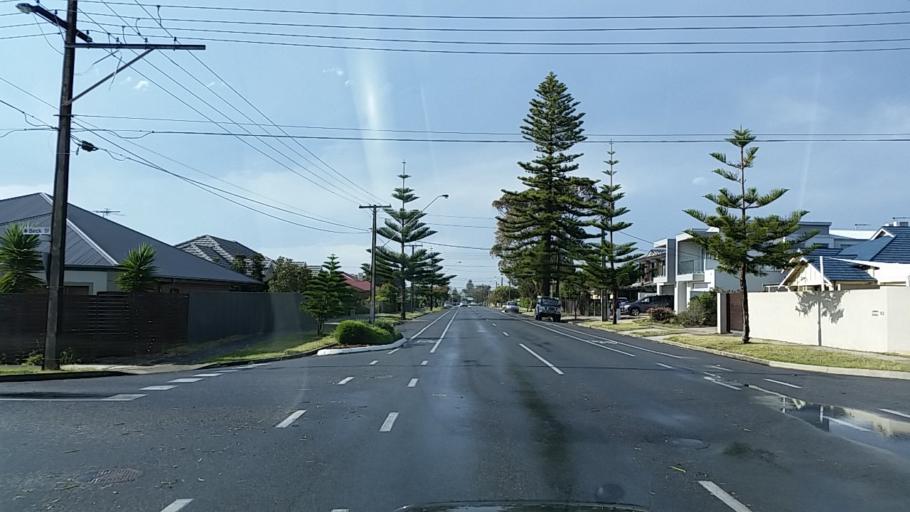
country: AU
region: South Australia
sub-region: Charles Sturt
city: Henley Beach
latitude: -34.9128
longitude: 138.4967
